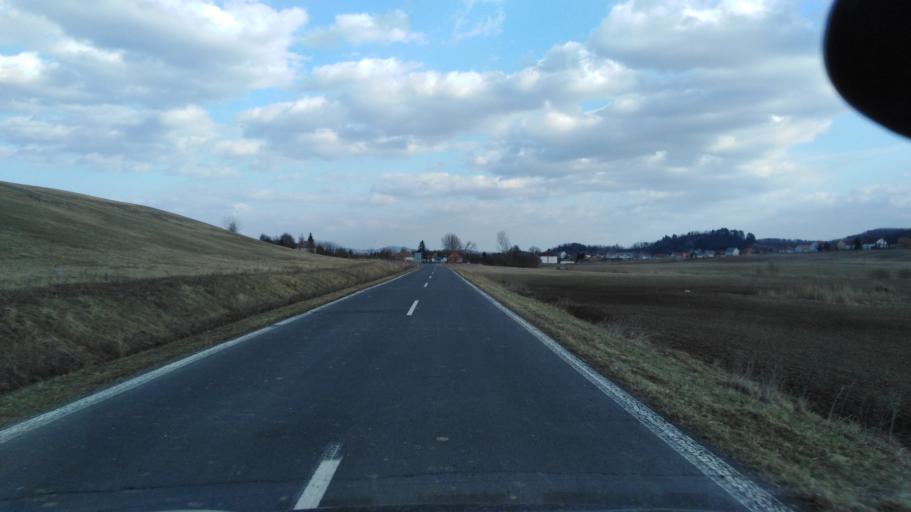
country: HU
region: Nograd
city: Matraterenye
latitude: 48.1518
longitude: 19.9462
